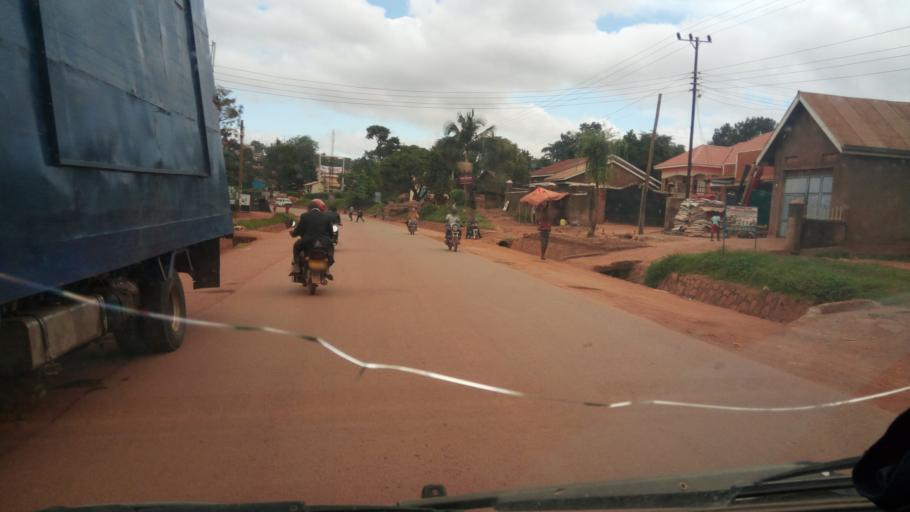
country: UG
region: Central Region
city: Kampala Central Division
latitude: 0.3351
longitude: 32.5487
